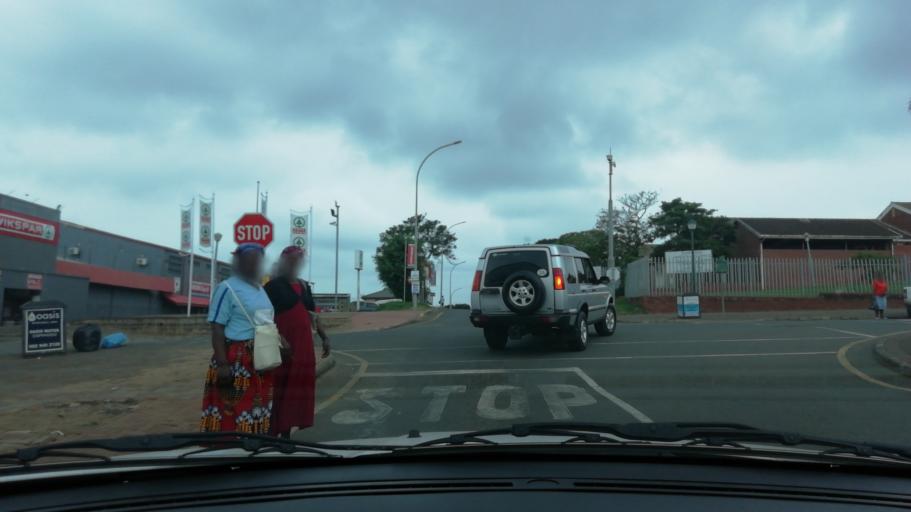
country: ZA
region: KwaZulu-Natal
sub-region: uThungulu District Municipality
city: Empangeni
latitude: -28.7425
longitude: 31.8921
